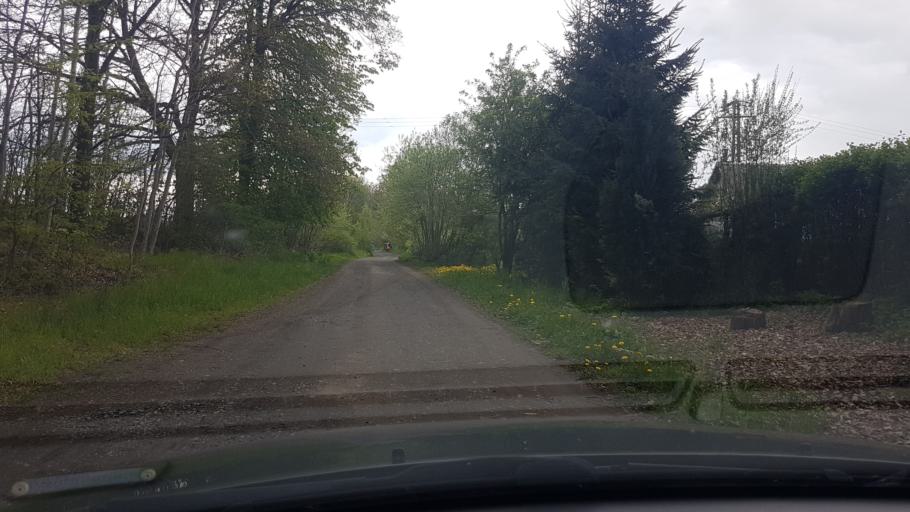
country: CZ
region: Karlovarsky
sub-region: Okres Cheb
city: Cheb
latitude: 50.0542
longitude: 12.3872
